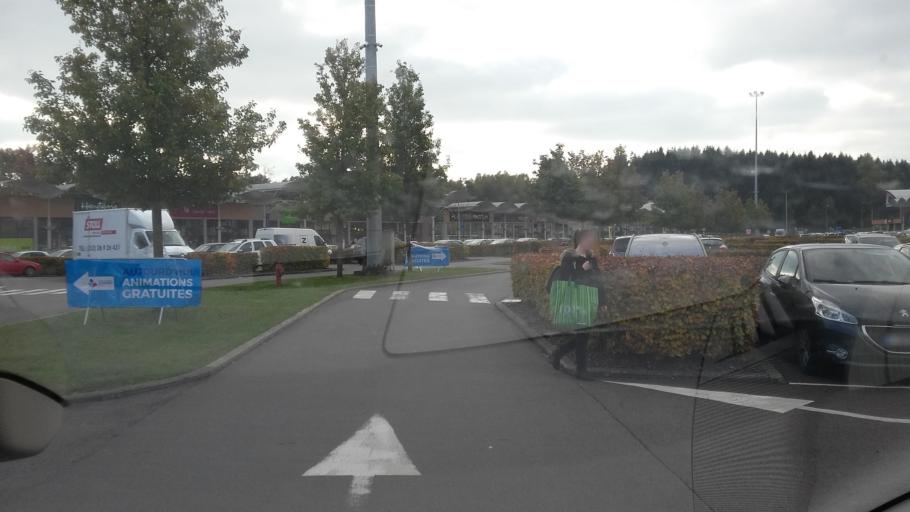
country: BE
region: Wallonia
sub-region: Province du Luxembourg
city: Arlon
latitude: 49.6838
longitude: 5.7899
